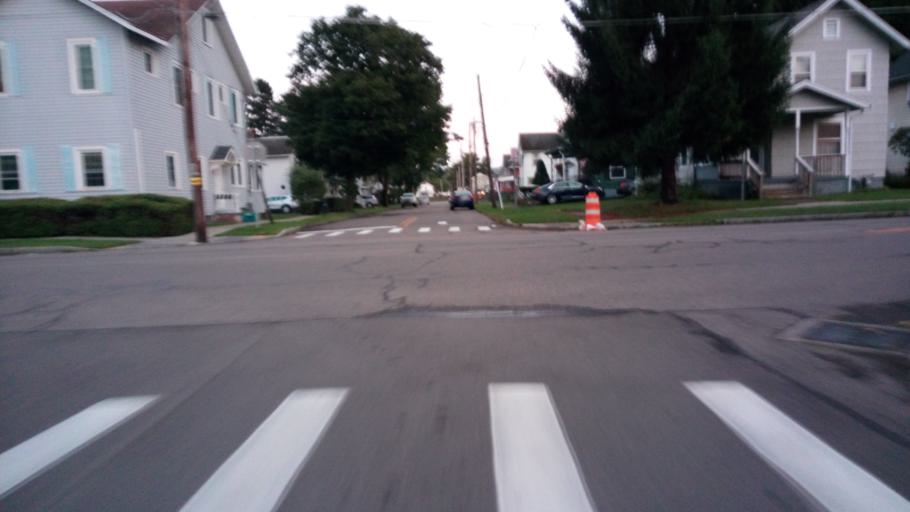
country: US
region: New York
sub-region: Chemung County
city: Elmira
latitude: 42.0969
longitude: -76.8216
